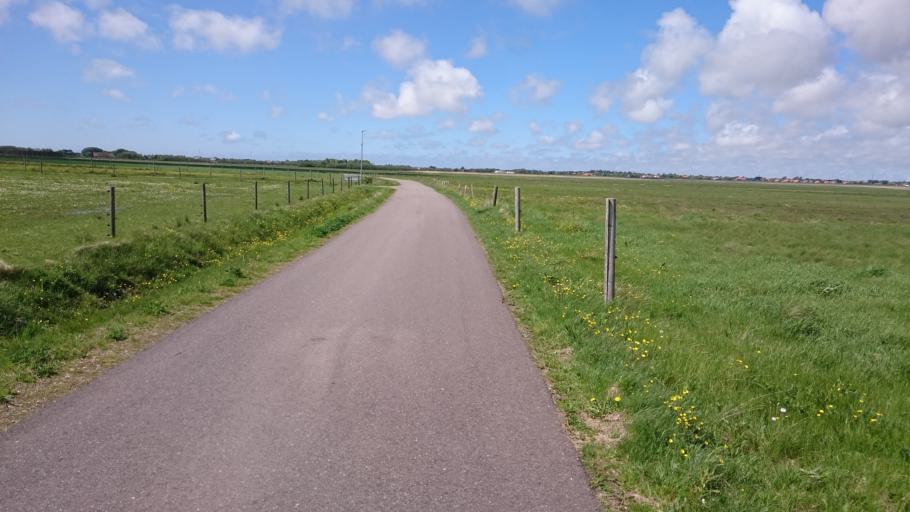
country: DK
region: South Denmark
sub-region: Fano Kommune
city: Nordby
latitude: 55.4241
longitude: 8.4141
